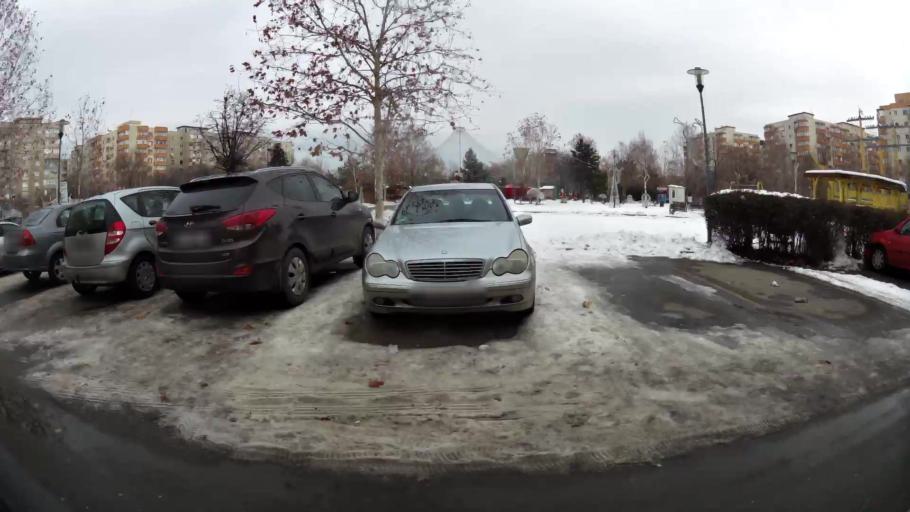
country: RO
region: Bucuresti
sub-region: Municipiul Bucuresti
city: Bucuresti
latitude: 44.4145
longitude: 26.0685
